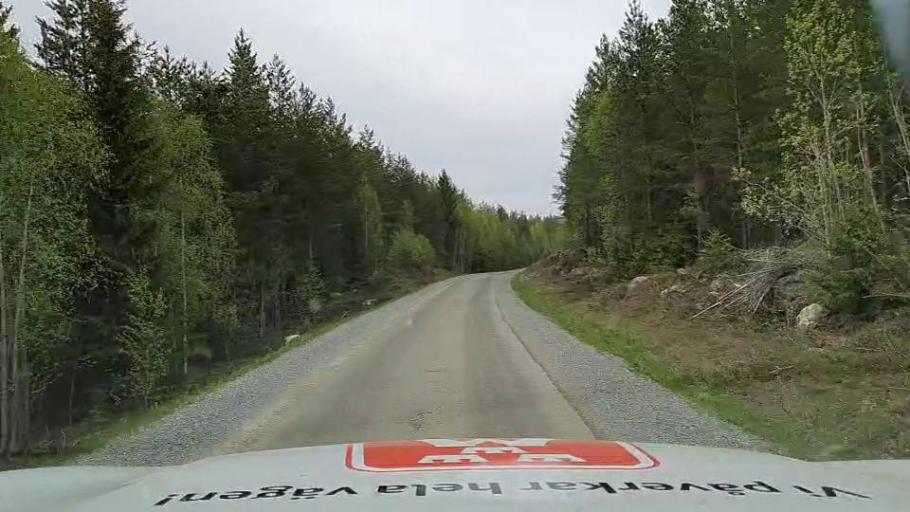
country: SE
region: Jaemtland
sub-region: Braecke Kommun
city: Braecke
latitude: 62.4700
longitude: 14.9161
